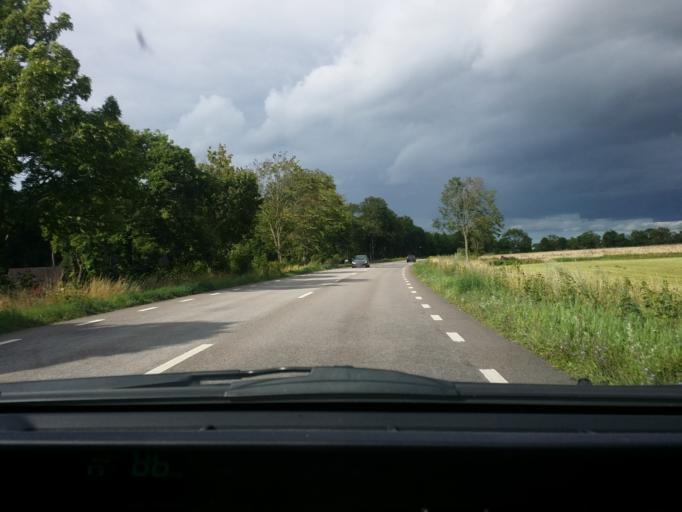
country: SE
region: Kalmar
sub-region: Borgholms Kommun
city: Borgholm
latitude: 56.9081
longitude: 16.7354
